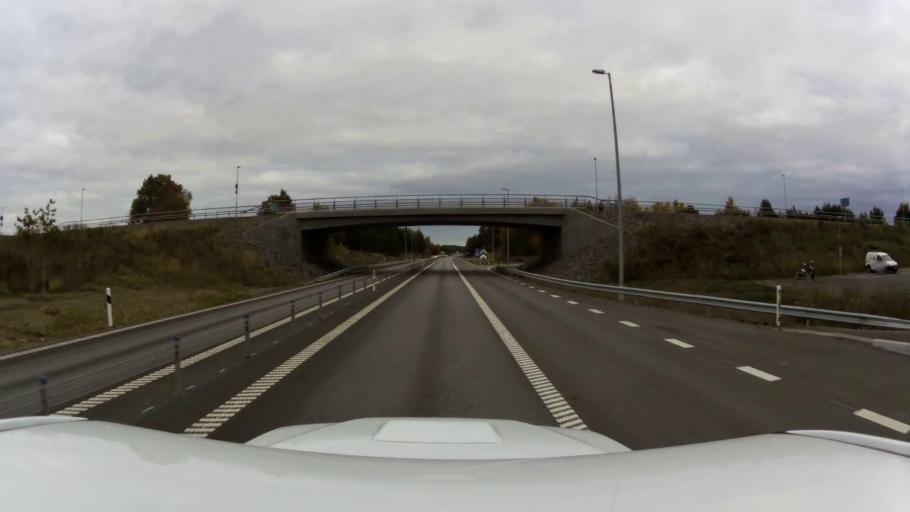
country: SE
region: OEstergoetland
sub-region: Linkopings Kommun
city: Ljungsbro
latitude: 58.4912
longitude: 15.4686
